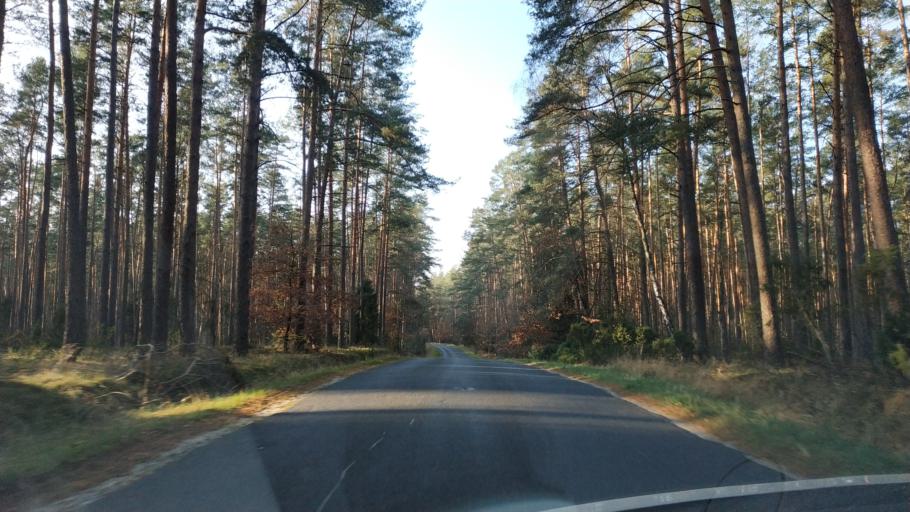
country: PL
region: Warmian-Masurian Voivodeship
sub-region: Powiat nowomiejski
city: Biskupiec
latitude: 53.4511
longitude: 19.4308
